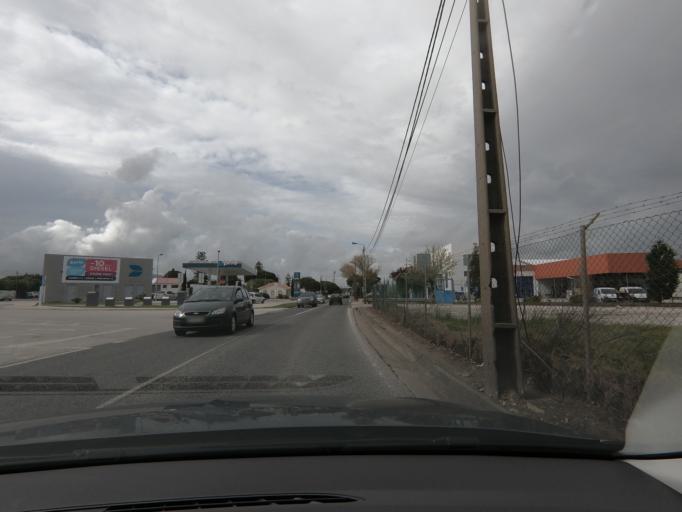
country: PT
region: Lisbon
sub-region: Sintra
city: Rio de Mouro
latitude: 38.7406
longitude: -9.3412
